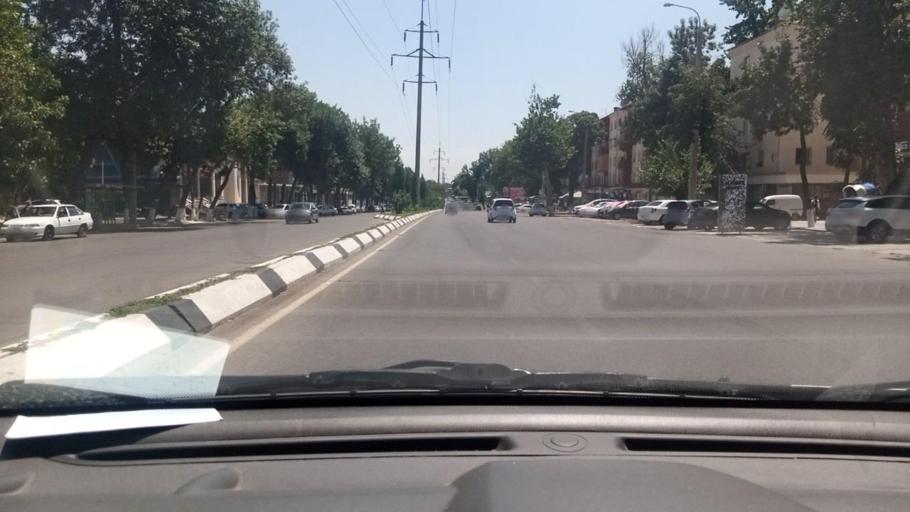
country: UZ
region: Toshkent Shahri
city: Tashkent
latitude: 41.2906
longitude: 69.1942
